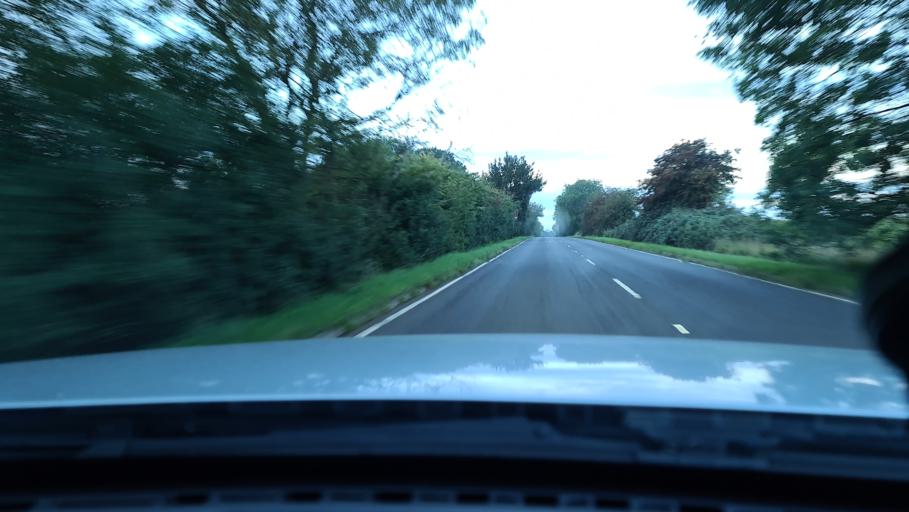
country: GB
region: England
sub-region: Warwickshire
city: Long Lawford
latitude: 52.4377
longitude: -1.3401
